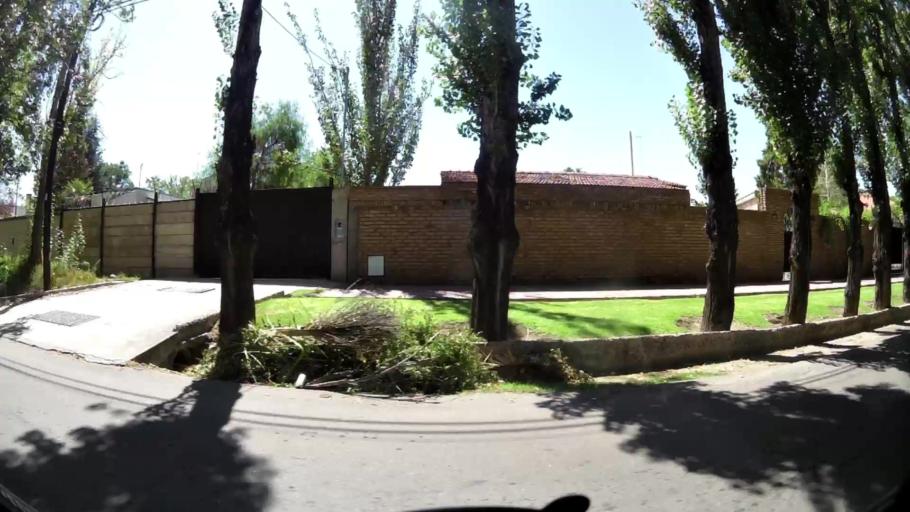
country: AR
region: Mendoza
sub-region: Departamento de Godoy Cruz
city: Godoy Cruz
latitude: -32.9643
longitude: -68.8634
